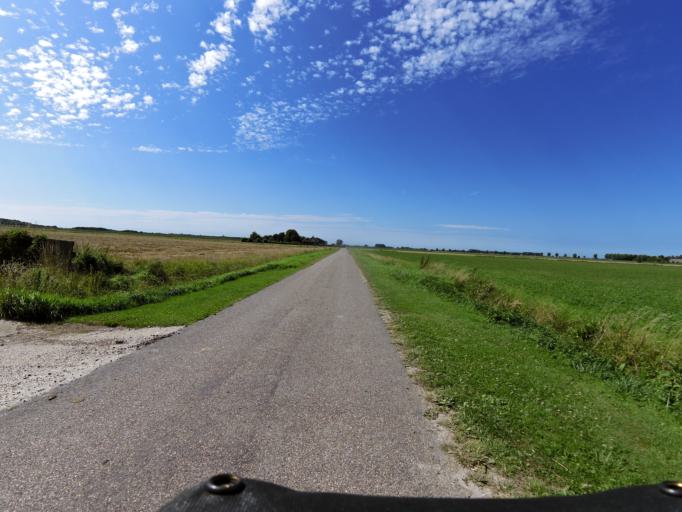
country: NL
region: Zeeland
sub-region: Gemeente Noord-Beveland
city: Kamperland
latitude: 51.5454
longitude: 3.7226
